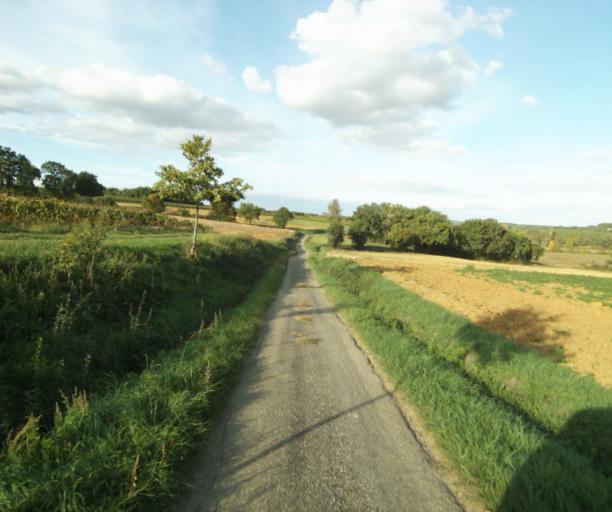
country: FR
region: Midi-Pyrenees
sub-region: Departement du Gers
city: Gondrin
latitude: 43.9001
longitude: 0.2860
